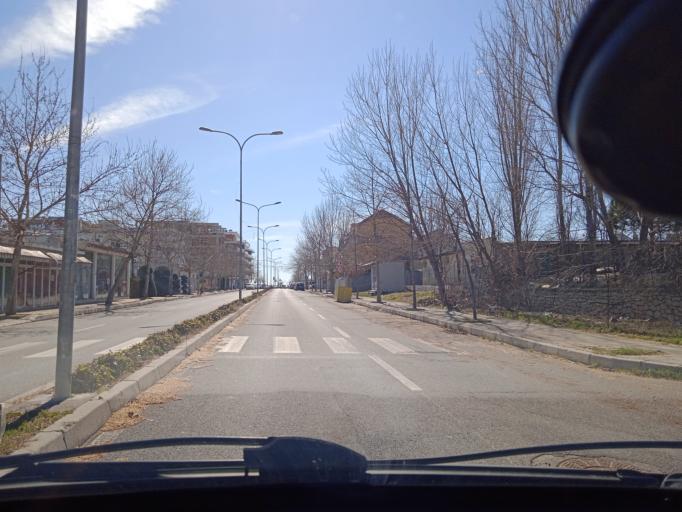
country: AL
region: Shkoder
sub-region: Rrethi i Shkodres
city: Velipoje
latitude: 41.8651
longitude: 19.4260
